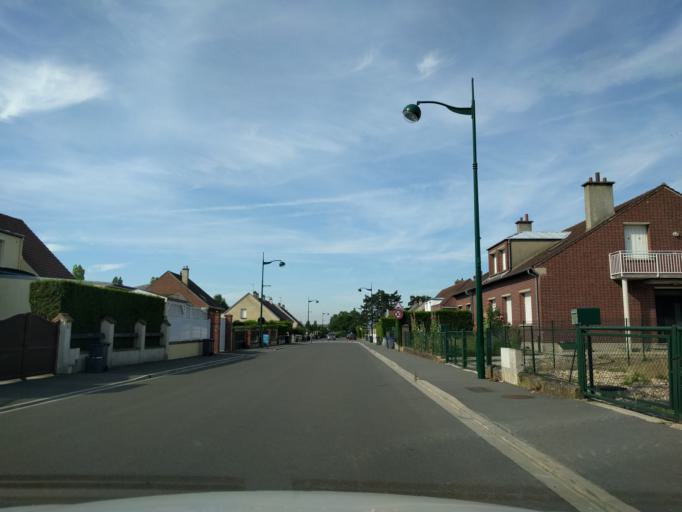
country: FR
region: Picardie
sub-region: Departement de l'Oise
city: Tille
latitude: 49.4618
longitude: 2.1101
